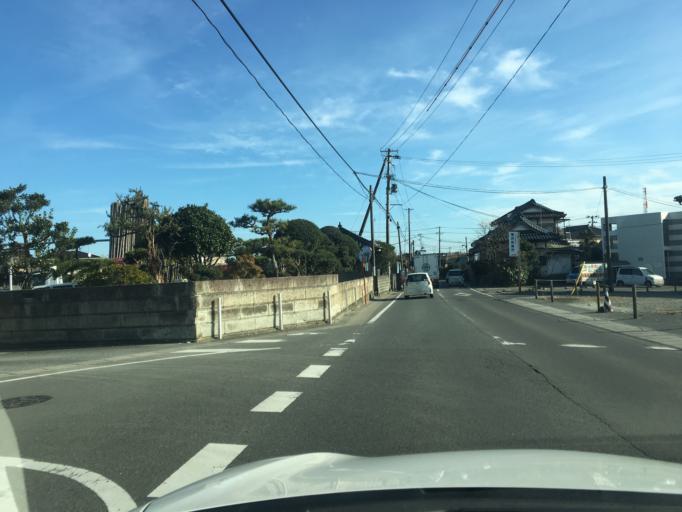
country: JP
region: Fukushima
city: Iwaki
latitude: 36.9538
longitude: 140.8695
